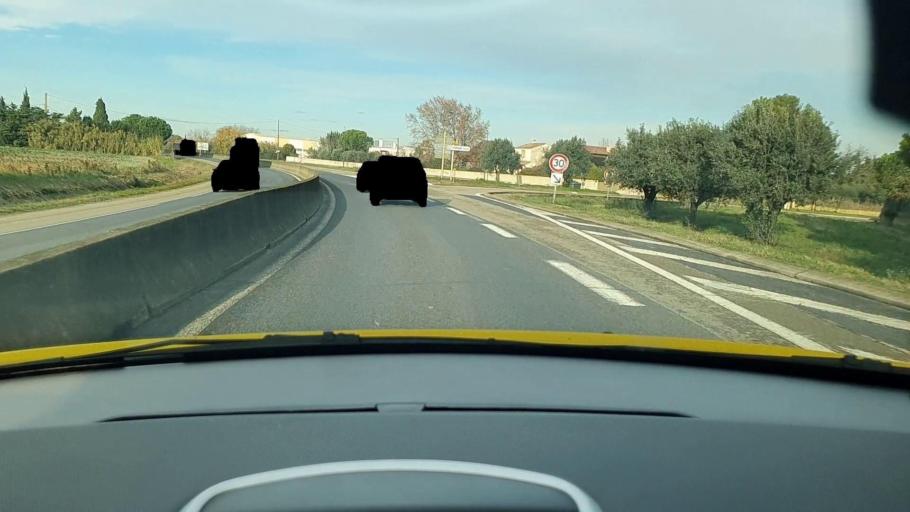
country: FR
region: Languedoc-Roussillon
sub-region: Departement du Gard
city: Fourques
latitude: 43.6932
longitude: 4.6033
